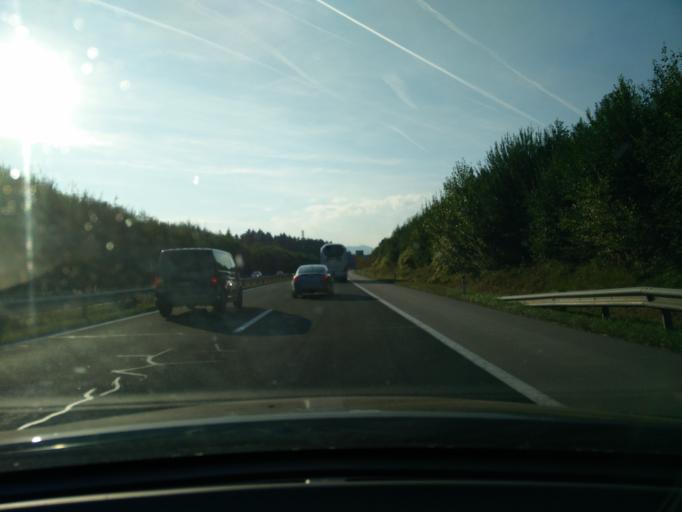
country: SI
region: Kranj
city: Kokrica
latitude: 46.2630
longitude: 14.3515
